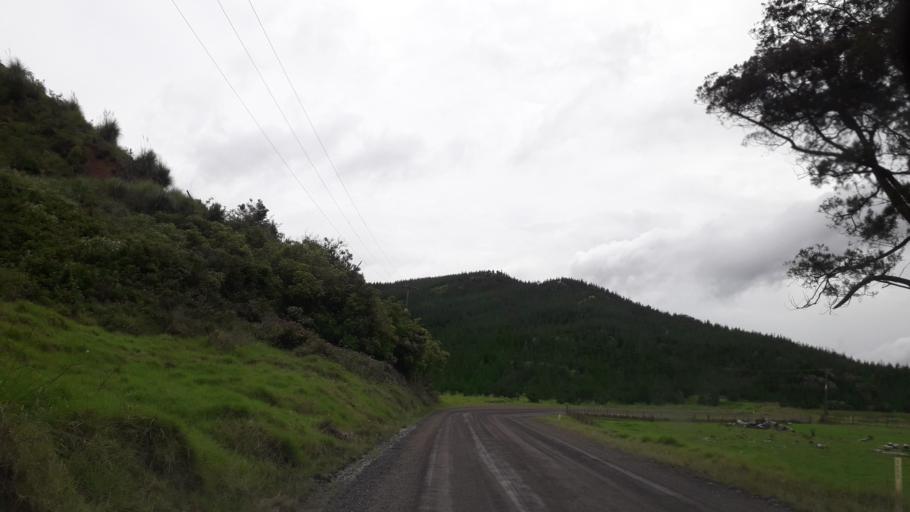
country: NZ
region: Northland
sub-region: Far North District
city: Ahipara
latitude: -35.4321
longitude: 173.3473
